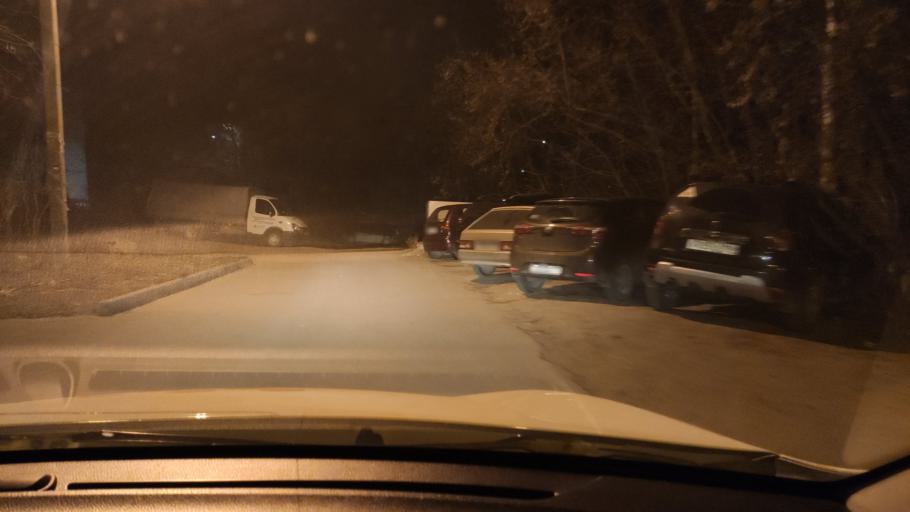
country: RU
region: Tatarstan
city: Vysokaya Gora
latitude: 55.8614
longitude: 49.2246
